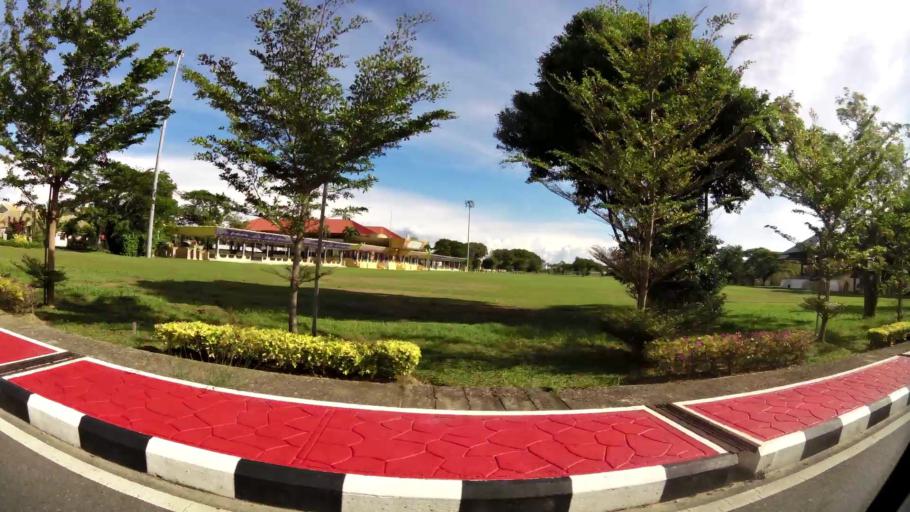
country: BN
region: Belait
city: Kuala Belait
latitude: 4.5885
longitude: 114.1908
